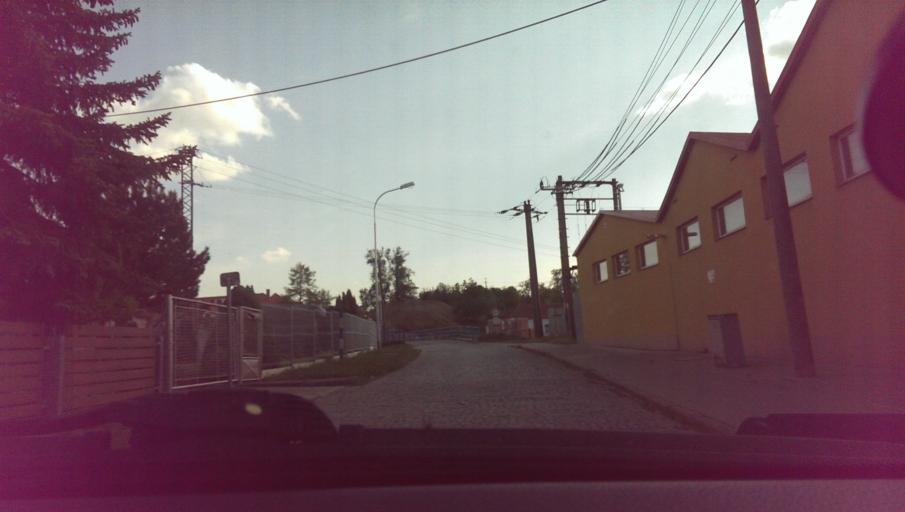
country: CZ
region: Zlin
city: Uhersky Brod
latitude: 49.0168
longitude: 17.6444
